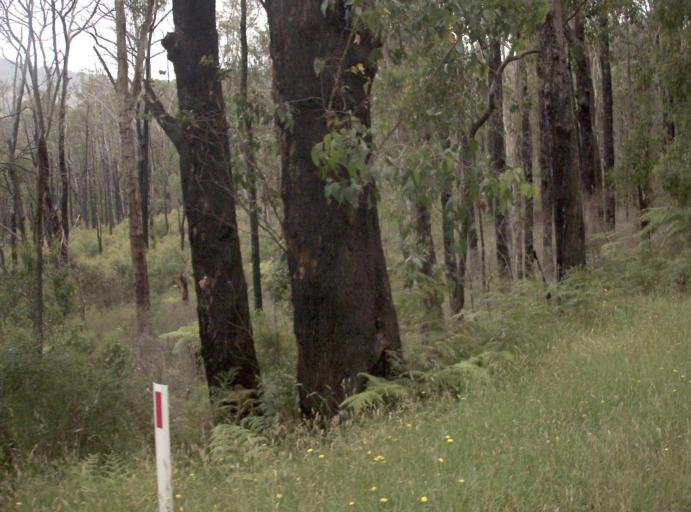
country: AU
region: Victoria
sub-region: Yarra Ranges
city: Healesville
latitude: -37.6306
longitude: 145.5928
